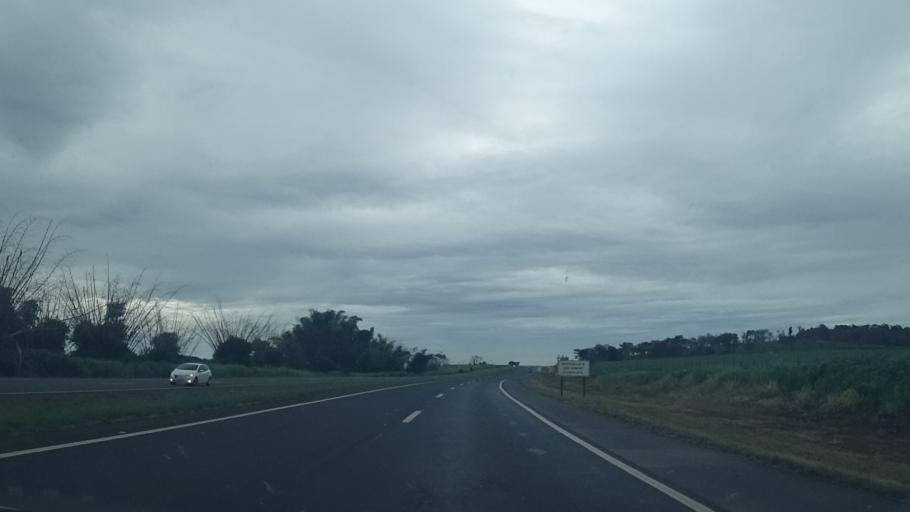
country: BR
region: Goias
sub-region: Goiatuba
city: Goiatuba
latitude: -18.0889
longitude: -49.2707
